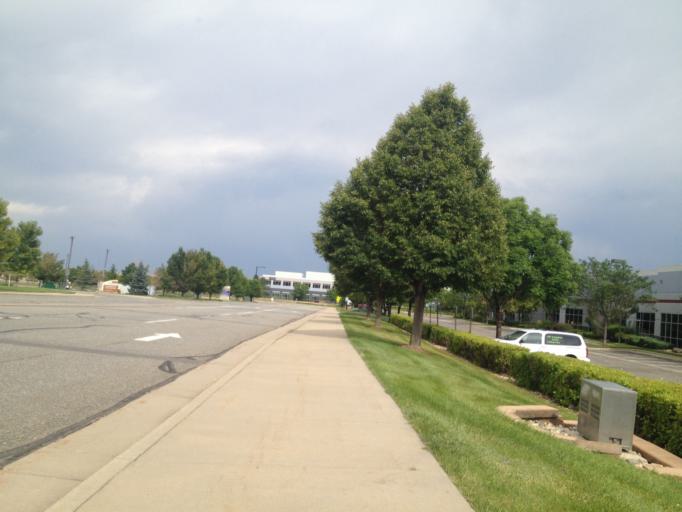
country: US
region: Colorado
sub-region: Boulder County
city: Lafayette
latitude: 39.9673
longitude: -105.0897
